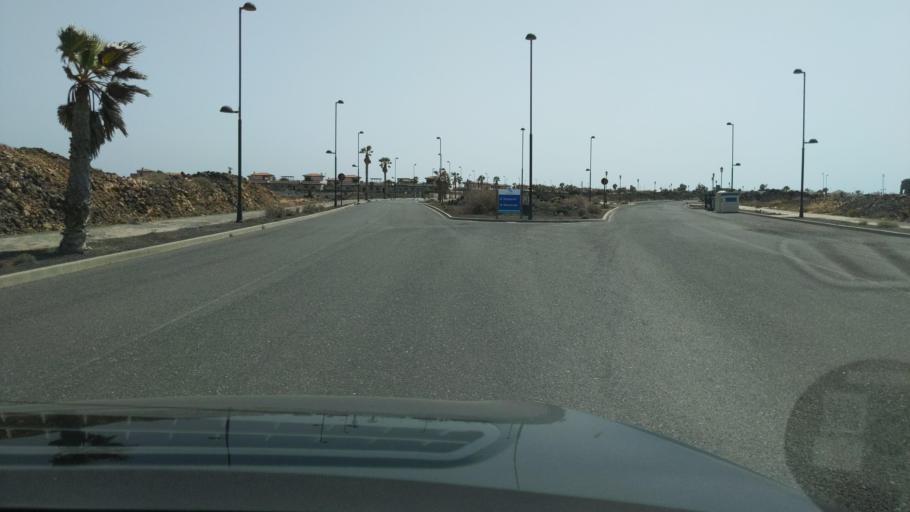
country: ES
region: Canary Islands
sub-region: Provincia de Las Palmas
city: Corralejo
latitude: 28.7346
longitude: -13.9454
